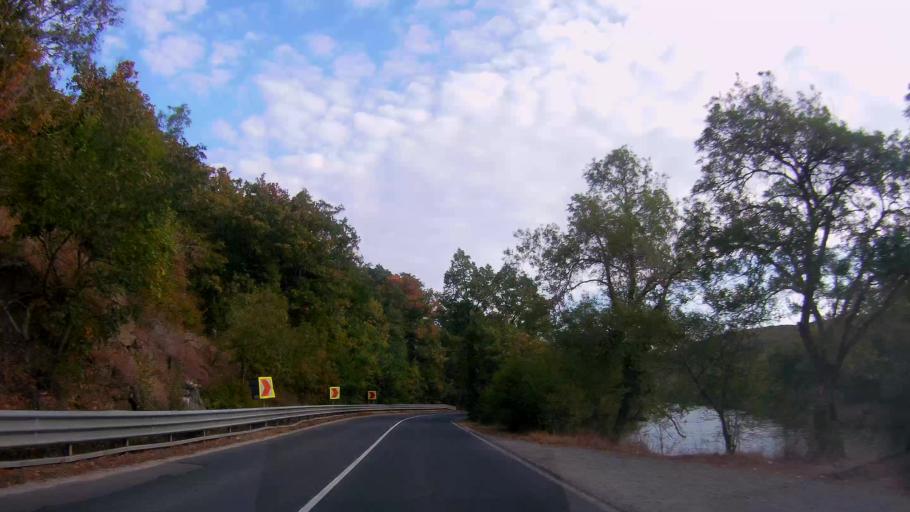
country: BG
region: Burgas
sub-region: Obshtina Primorsko
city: Primorsko
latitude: 42.3051
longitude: 27.7223
